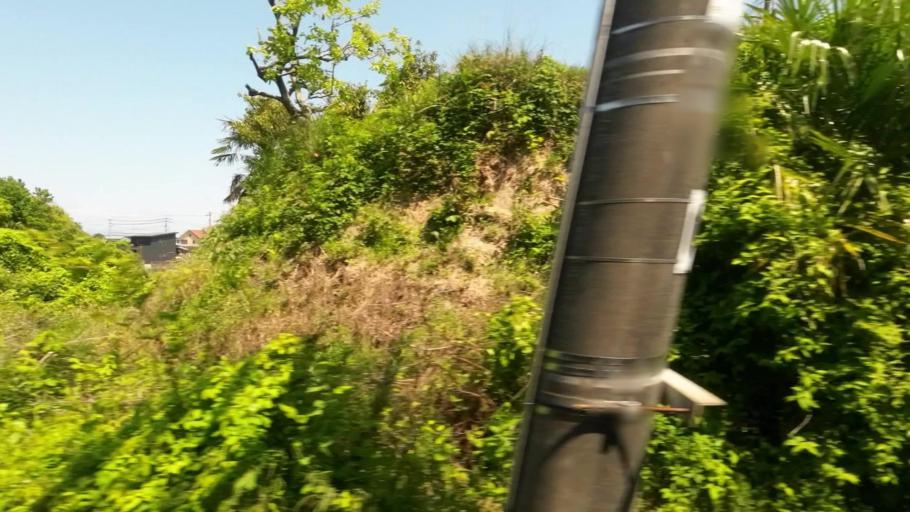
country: JP
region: Ehime
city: Hojo
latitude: 34.0568
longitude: 132.8845
